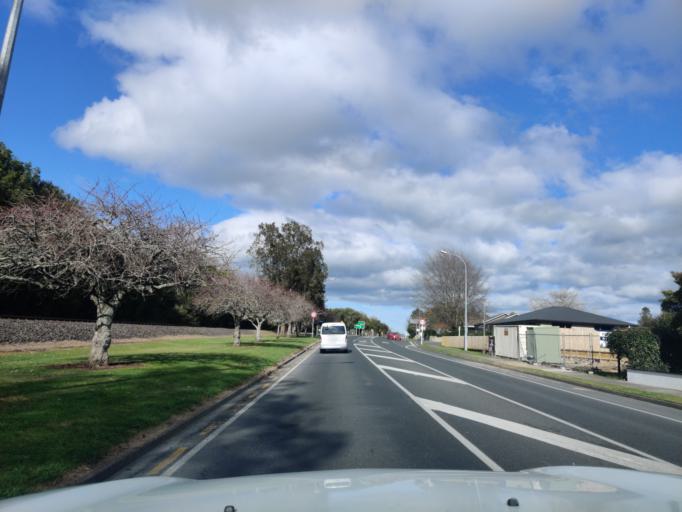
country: NZ
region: Waikato
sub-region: Matamata-Piako District
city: Matamata
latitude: -37.8224
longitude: 175.7710
